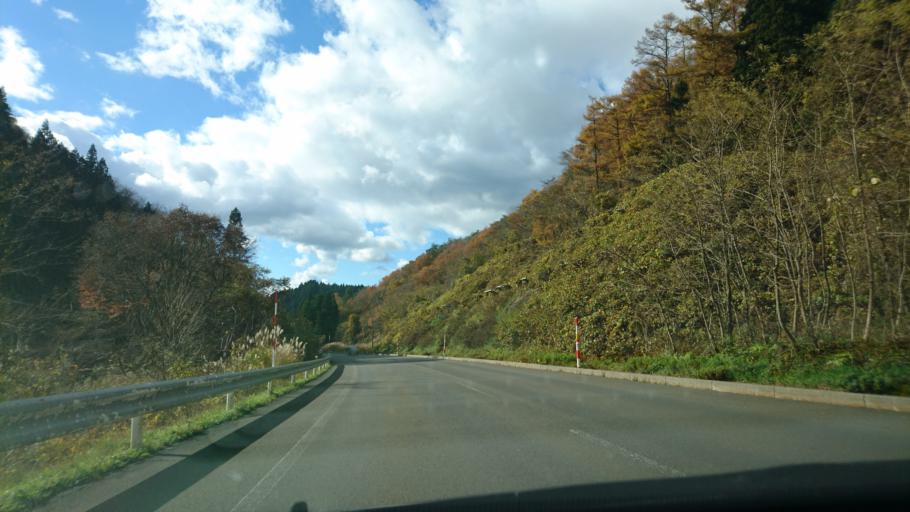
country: JP
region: Akita
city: Yuzawa
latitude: 39.2874
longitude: 140.3095
